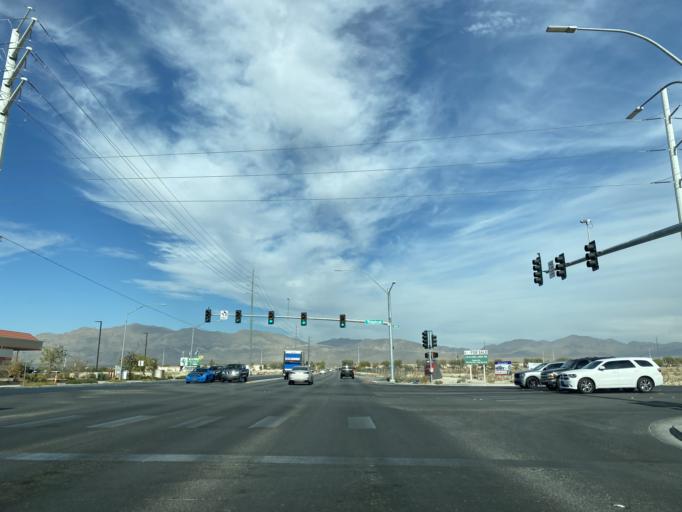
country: US
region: Nevada
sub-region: Clark County
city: Nellis Air Force Base
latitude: 36.2686
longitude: -115.1169
